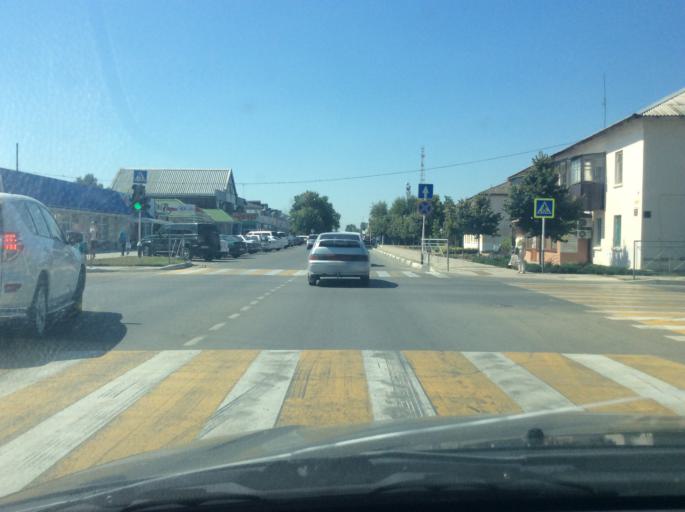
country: RU
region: Krasnodarskiy
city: Slavyansk-na-Kubani
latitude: 45.2540
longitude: 38.1175
